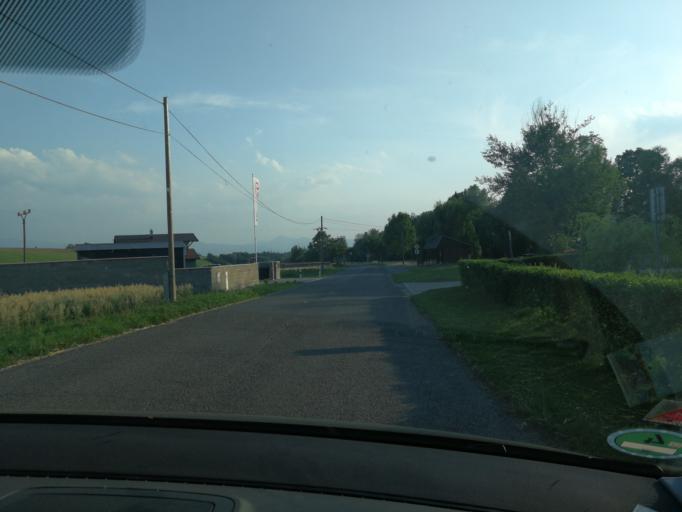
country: SK
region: Zilinsky
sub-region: Okres Liptovsky Mikulas
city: Liptovsky Mikulas
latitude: 49.1616
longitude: 19.5391
